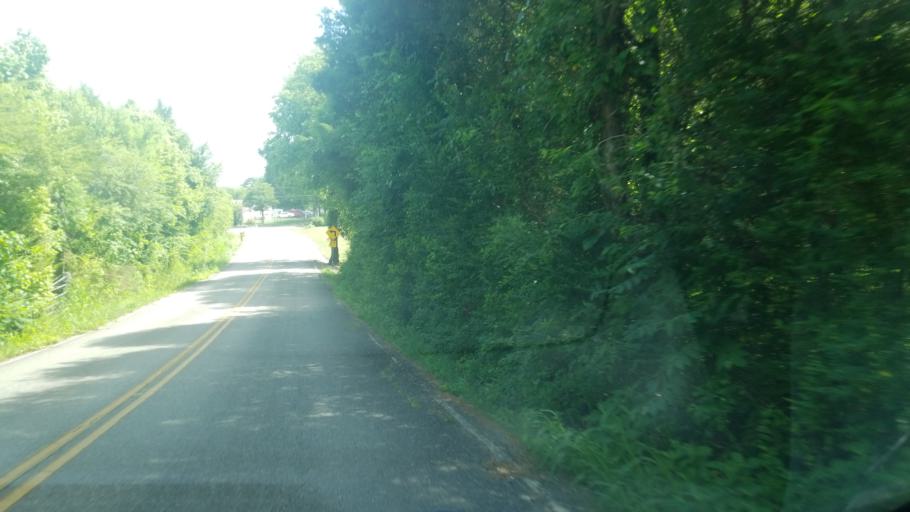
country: US
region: Tennessee
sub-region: Hamilton County
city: Lakesite
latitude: 35.2351
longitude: -85.0139
